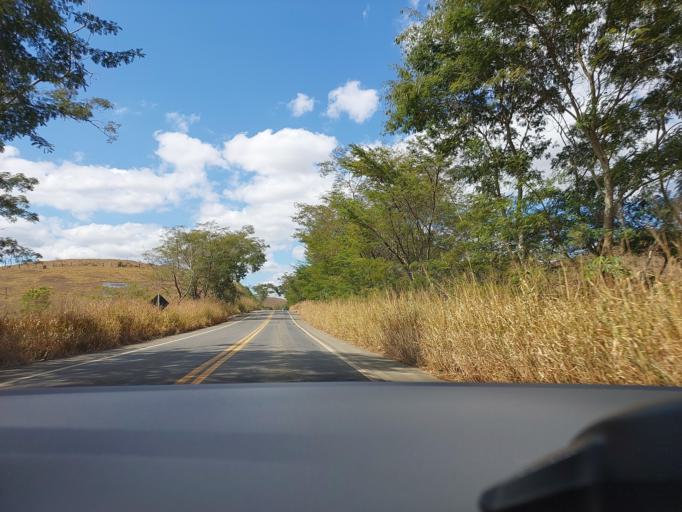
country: BR
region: Minas Gerais
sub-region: Muriae
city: Muriae
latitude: -21.1491
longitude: -42.1581
